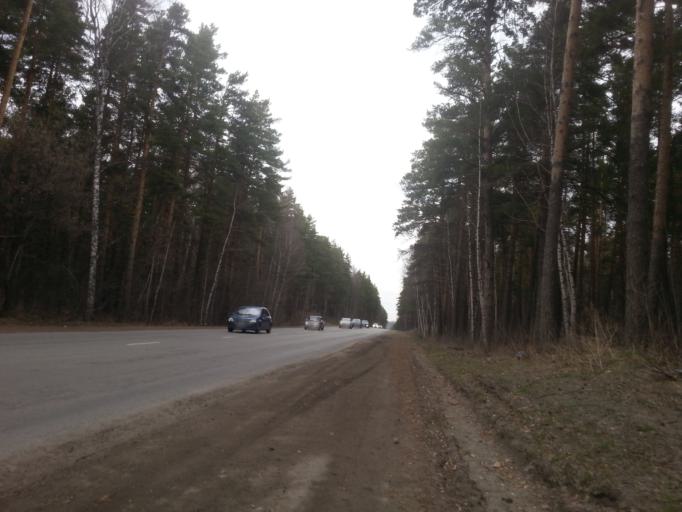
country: RU
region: Altai Krai
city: Yuzhnyy
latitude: 53.2802
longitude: 83.7173
